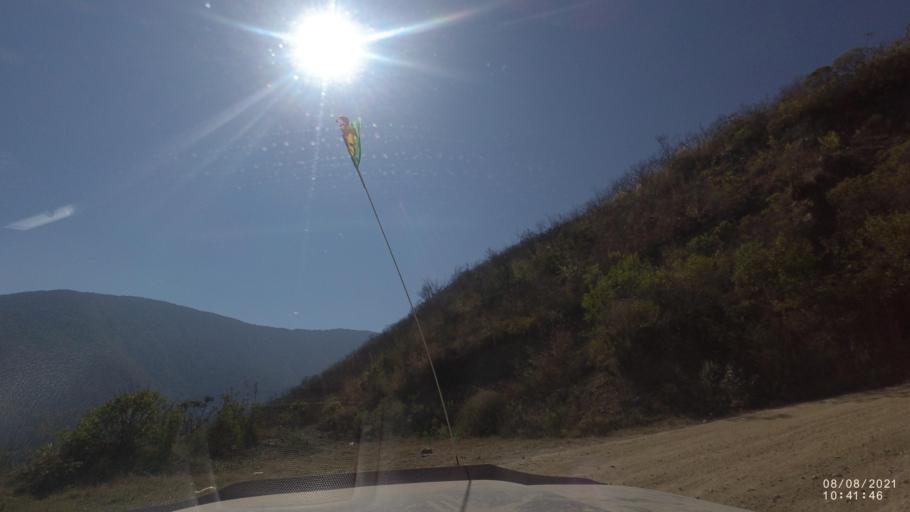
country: BO
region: La Paz
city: Quime
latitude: -16.6981
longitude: -66.7229
